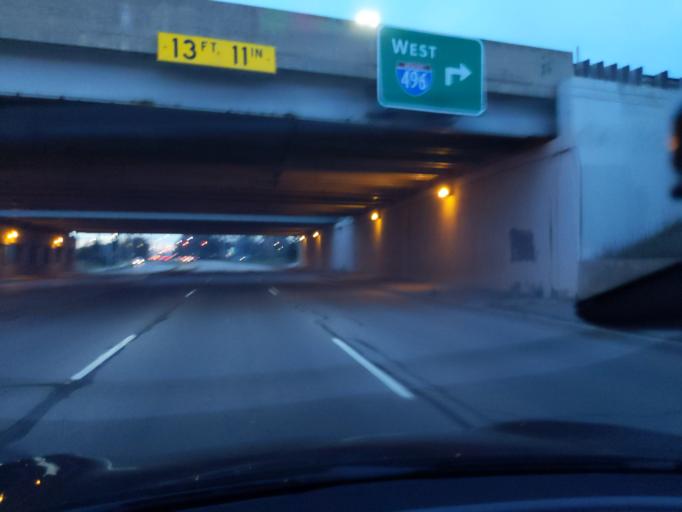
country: US
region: Michigan
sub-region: Ingham County
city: Lansing
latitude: 42.7252
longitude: -84.5450
